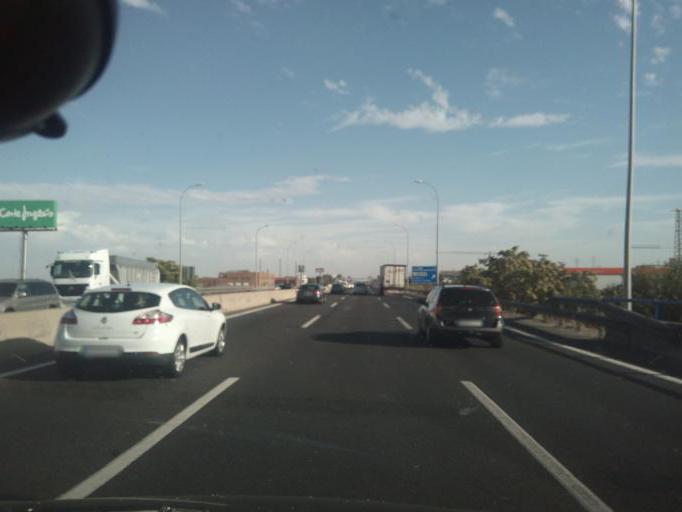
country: ES
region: Madrid
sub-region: Provincia de Madrid
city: Valdemoro
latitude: 40.2171
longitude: -3.6845
